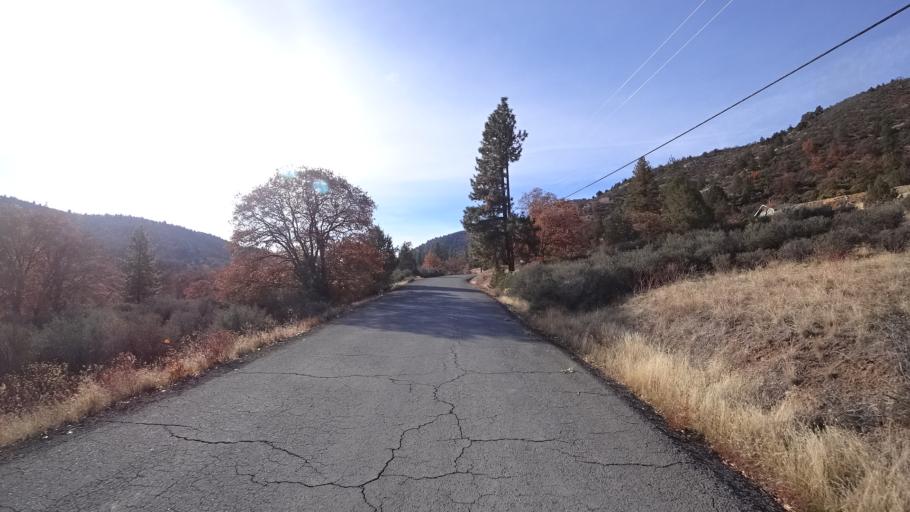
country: US
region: California
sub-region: Siskiyou County
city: Montague
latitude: 41.6201
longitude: -122.5771
